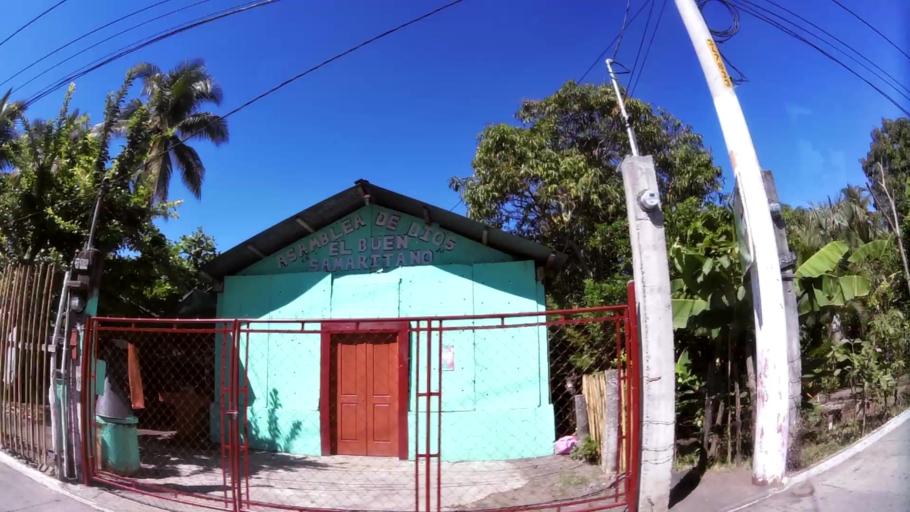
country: GT
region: Escuintla
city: Iztapa
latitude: 13.9326
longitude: -90.7090
